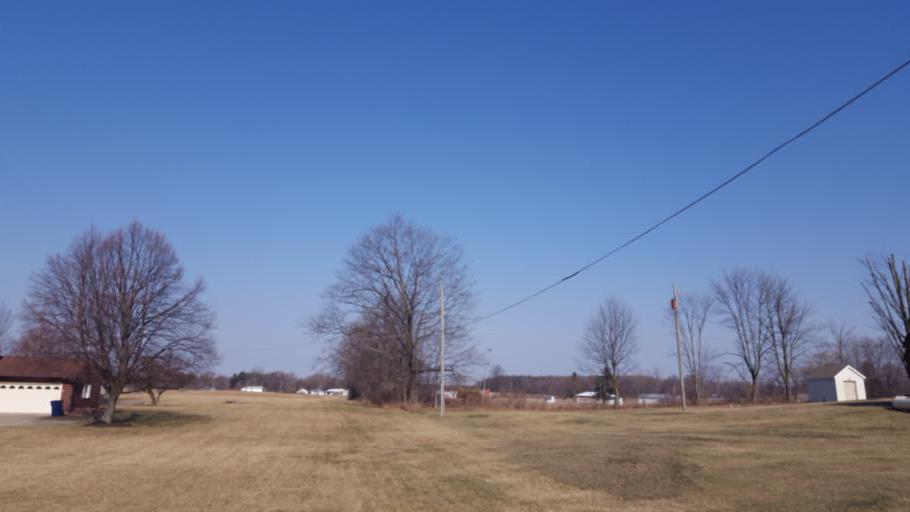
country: US
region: Ohio
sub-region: Richland County
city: Shelby
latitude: 40.8431
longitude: -82.6196
